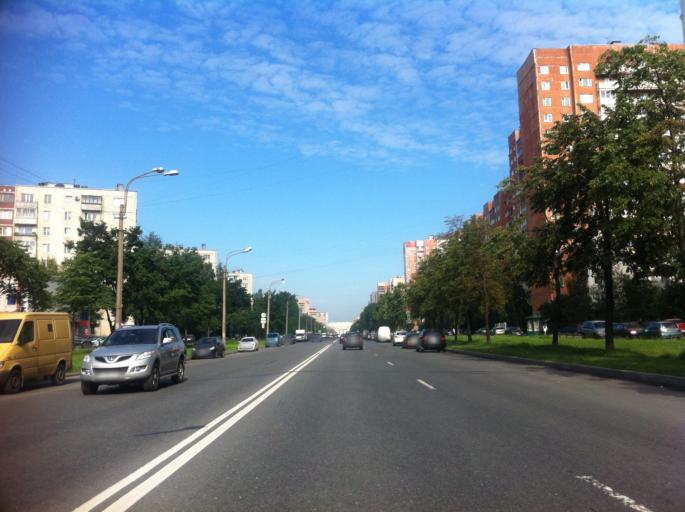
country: RU
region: St.-Petersburg
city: Uritsk
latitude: 59.8493
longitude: 30.2129
